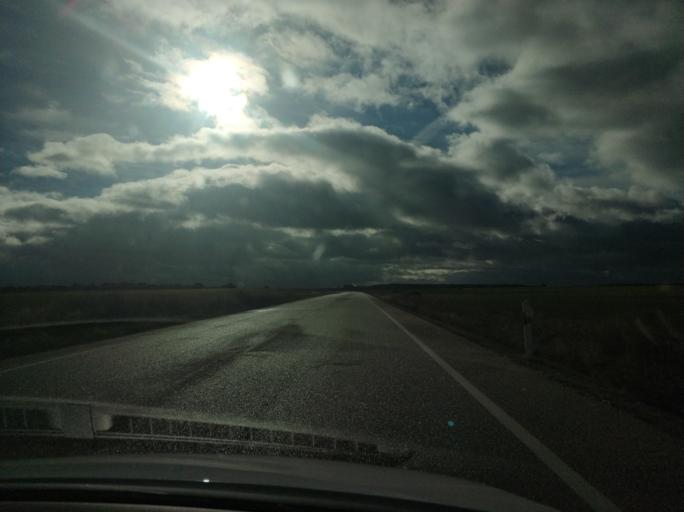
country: ES
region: Castille and Leon
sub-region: Provincia de Segovia
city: Corral de Ayllon
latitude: 41.3991
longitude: -3.4255
